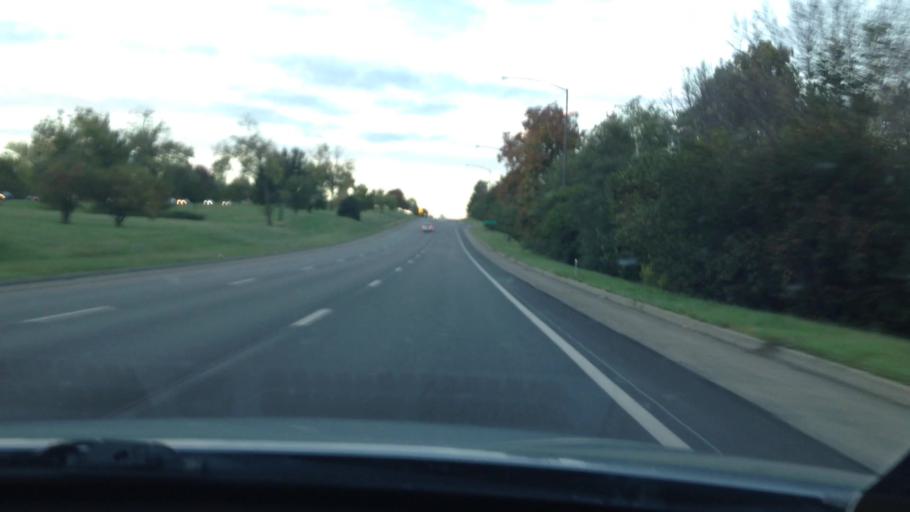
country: US
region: Kansas
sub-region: Johnson County
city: Mission Hills
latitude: 39.0205
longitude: -94.5537
